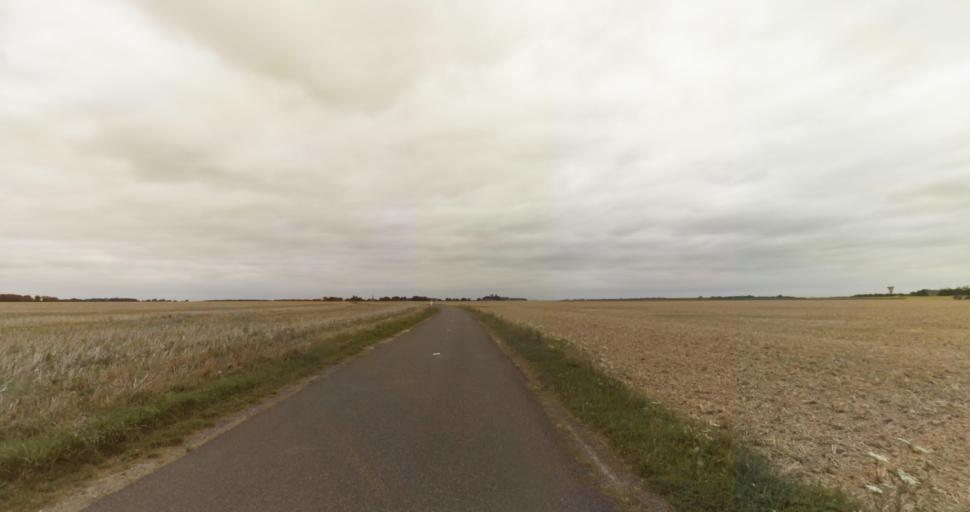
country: FR
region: Haute-Normandie
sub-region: Departement de l'Eure
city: Marcilly-sur-Eure
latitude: 48.9177
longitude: 1.2738
